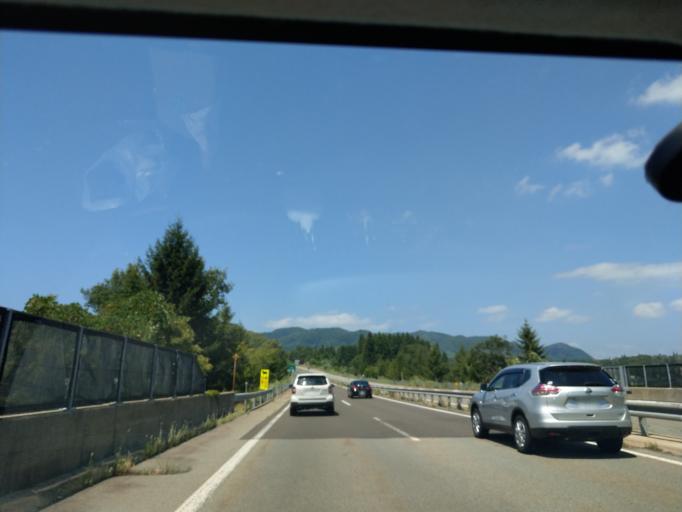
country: JP
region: Akita
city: Omagari
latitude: 39.4176
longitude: 140.4361
